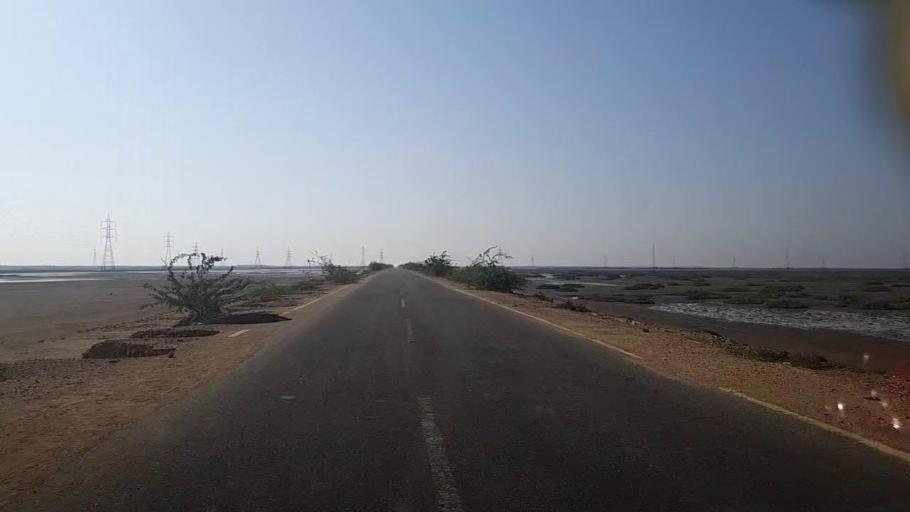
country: PK
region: Sindh
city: Mirpur Sakro
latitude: 24.5981
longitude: 67.4982
